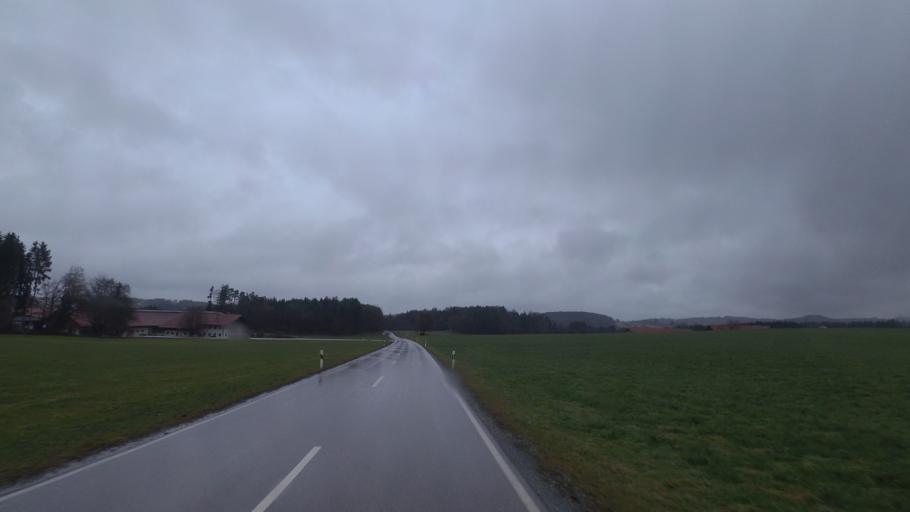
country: DE
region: Bavaria
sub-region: Upper Bavaria
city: Sankt Leonhard am Wonneberg
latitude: 47.9336
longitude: 12.6794
